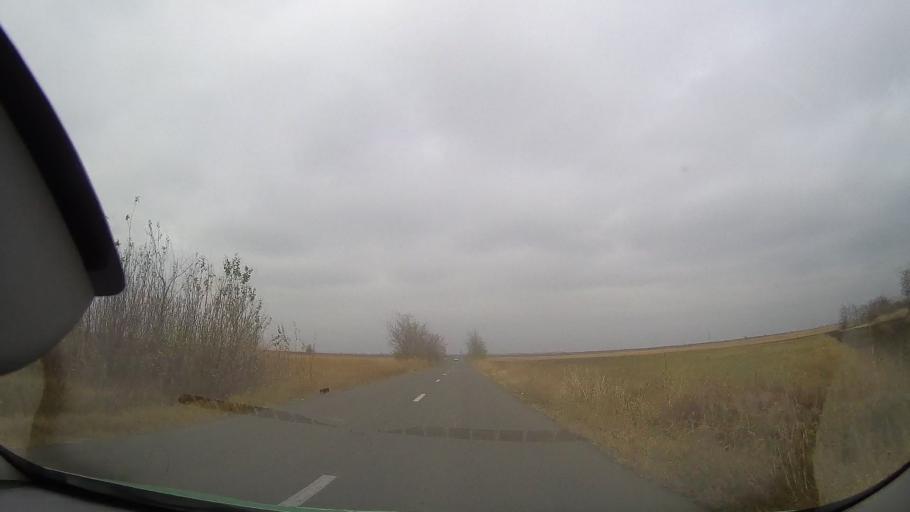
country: RO
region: Buzau
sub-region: Comuna Scutelnici
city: Scutelnici
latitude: 44.8831
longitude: 26.8761
